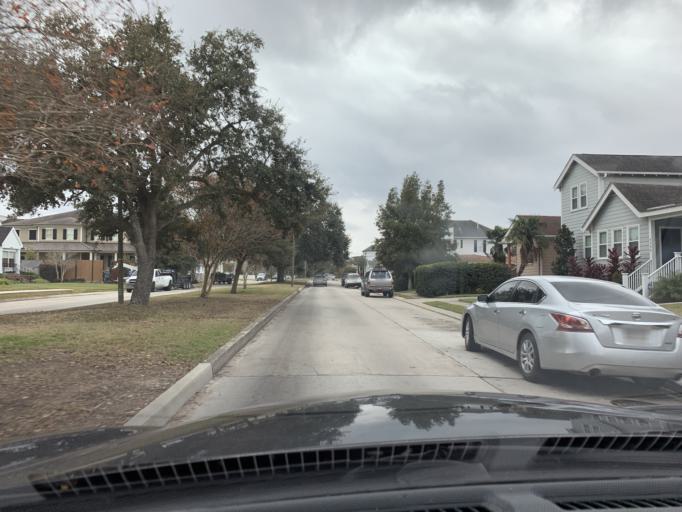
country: US
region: Louisiana
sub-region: Jefferson Parish
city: Metairie
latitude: 30.0091
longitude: -90.1022
